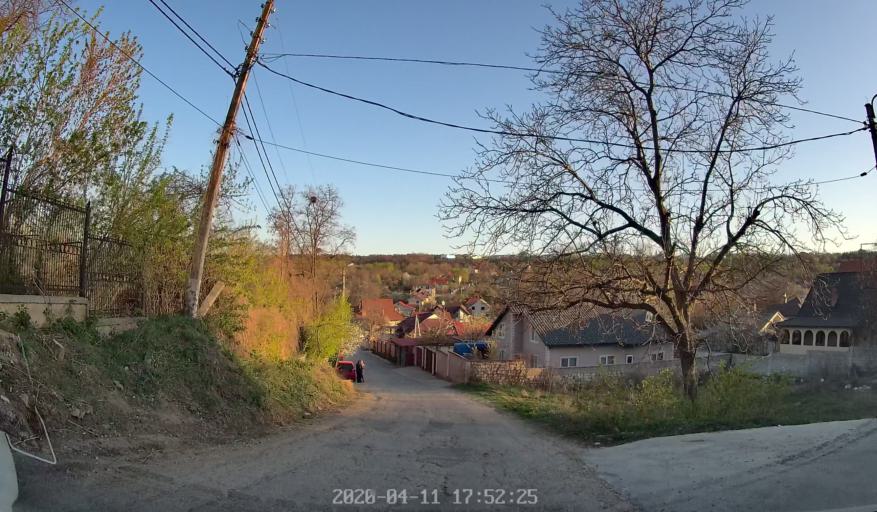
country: MD
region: Chisinau
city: Chisinau
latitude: 46.9730
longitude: 28.8640
